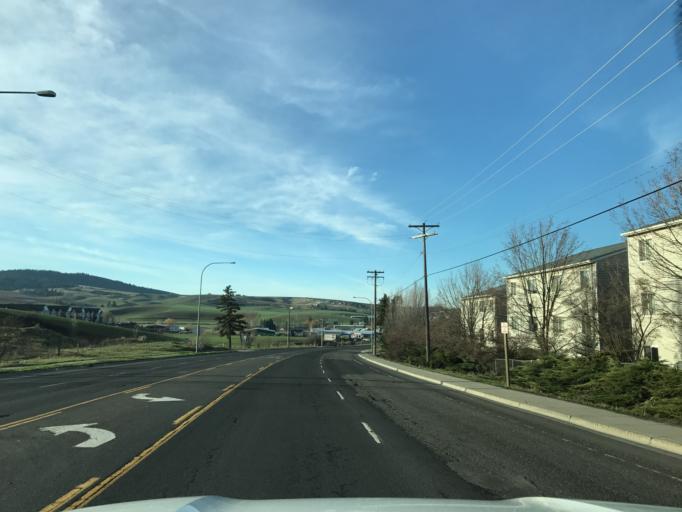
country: US
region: Idaho
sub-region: Latah County
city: Moscow
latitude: 46.7208
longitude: -117.0015
